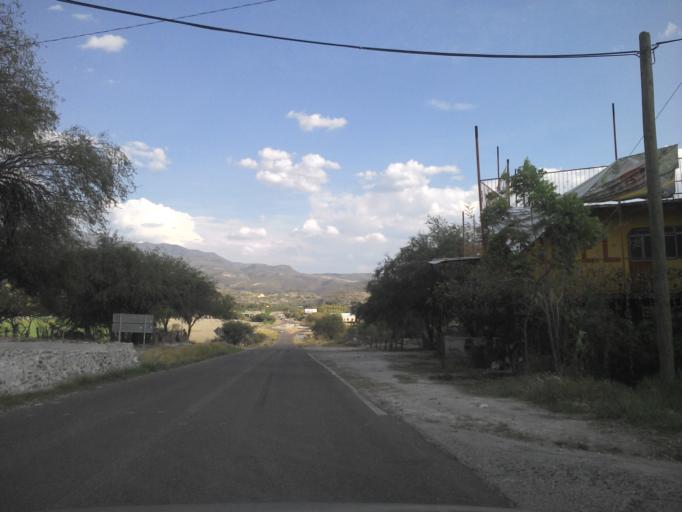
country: MX
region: Zacatecas
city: Juchipila
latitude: 21.2679
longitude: -103.1634
